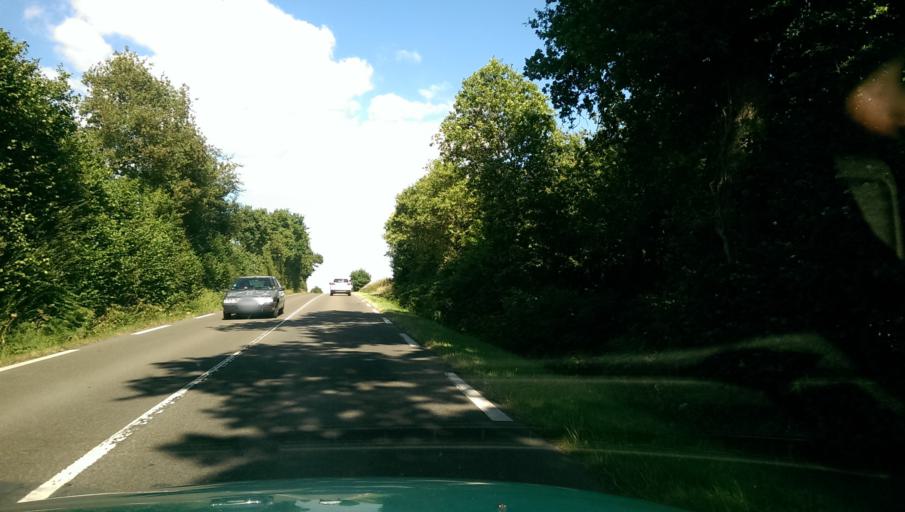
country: FR
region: Pays de la Loire
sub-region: Departement de la Loire-Atlantique
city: Lege
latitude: 46.8833
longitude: -1.6302
